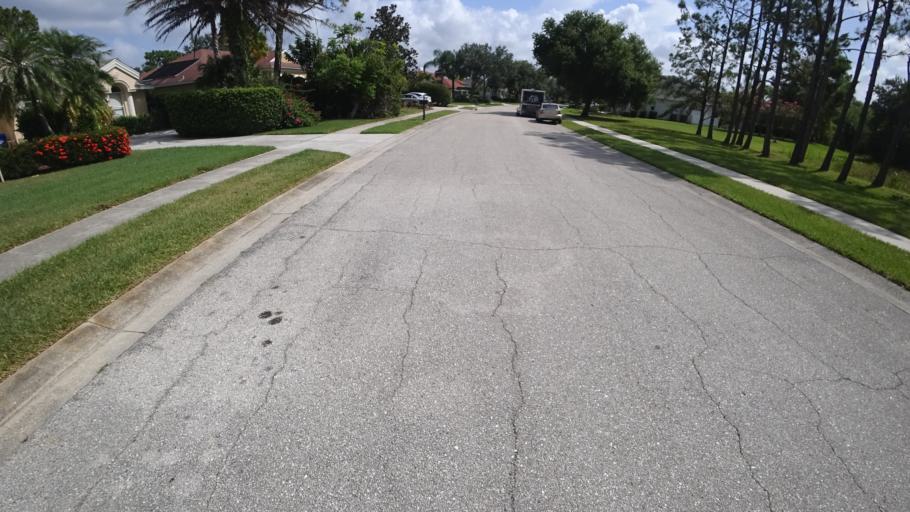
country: US
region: Florida
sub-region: Sarasota County
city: The Meadows
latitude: 27.4115
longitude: -82.4431
